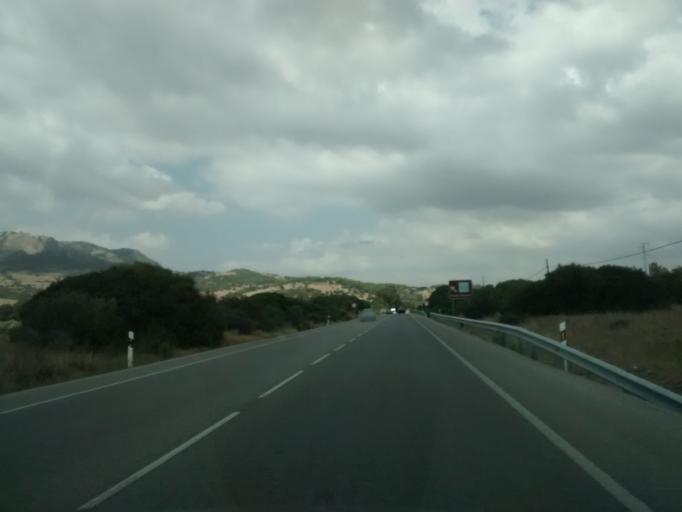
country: ES
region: Andalusia
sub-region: Provincia de Cadiz
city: Tarifa
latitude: 36.0744
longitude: -5.6875
